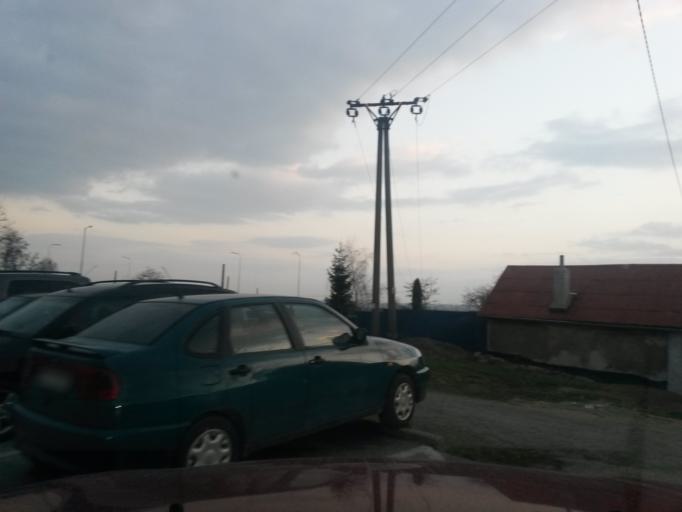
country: SK
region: Kosicky
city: Kosice
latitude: 48.7609
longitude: 21.2596
